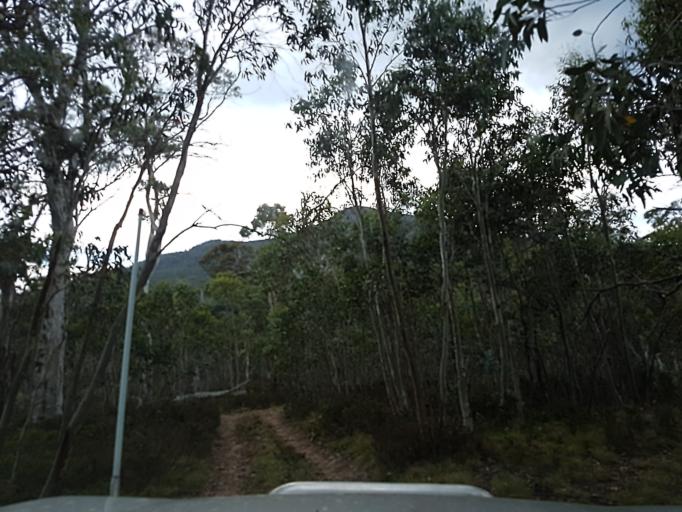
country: AU
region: New South Wales
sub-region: Snowy River
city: Jindabyne
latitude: -36.8803
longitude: 148.1598
